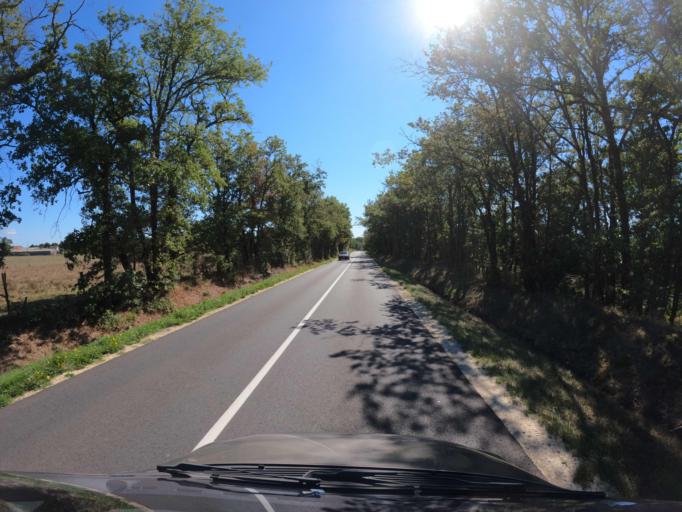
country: FR
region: Poitou-Charentes
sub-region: Departement de la Vienne
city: Lathus-Saint-Remy
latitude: 46.3707
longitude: 0.9336
